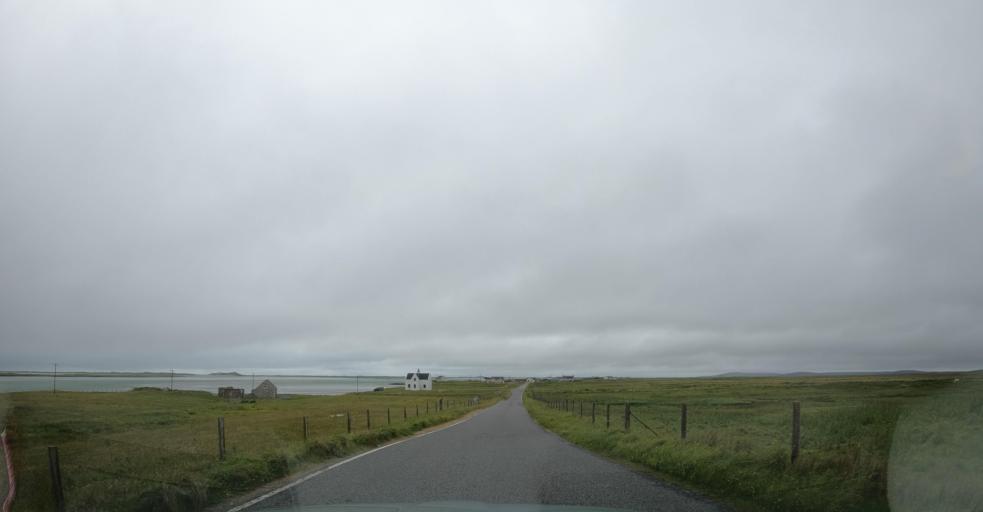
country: GB
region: Scotland
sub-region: Eilean Siar
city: Isle of North Uist
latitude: 57.5578
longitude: -7.3630
